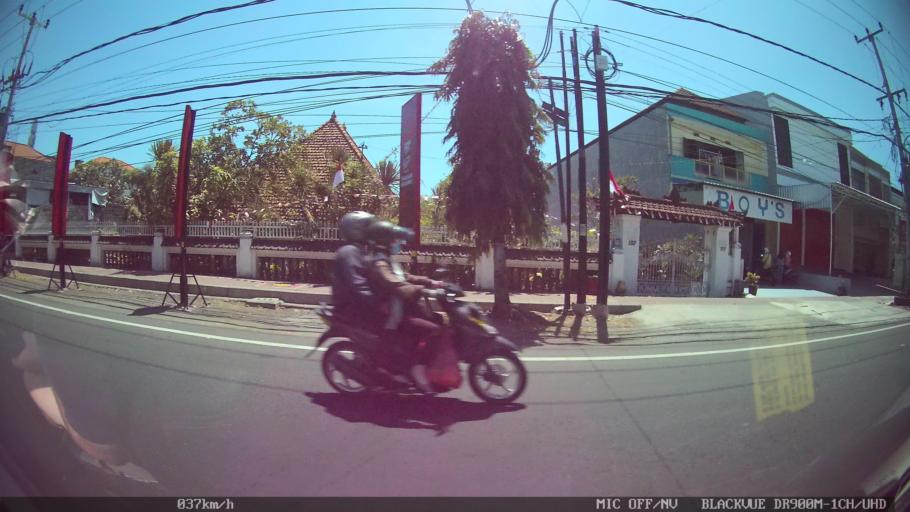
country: ID
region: Bali
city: Banjar Kaliuntu Satu
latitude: -8.1135
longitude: 115.0823
